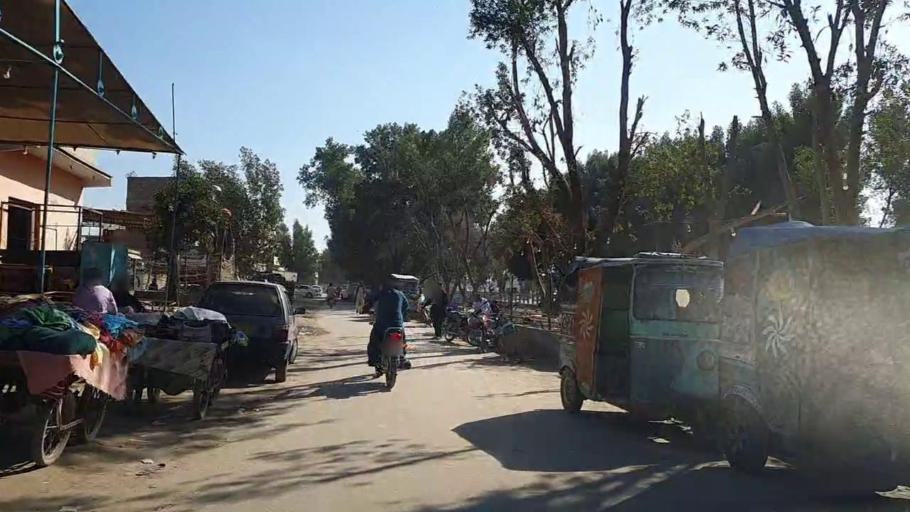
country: PK
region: Sindh
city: Nawabshah
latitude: 26.2524
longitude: 68.4196
